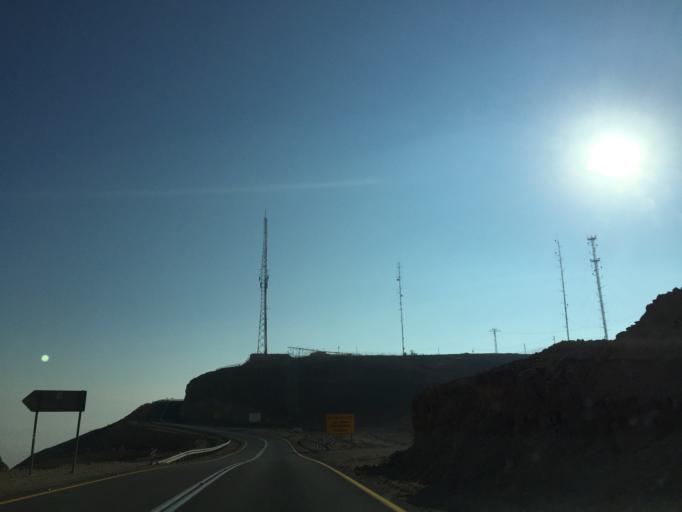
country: JO
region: Ma'an
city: Al Quwayrah
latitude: 30.0212
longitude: 35.0569
